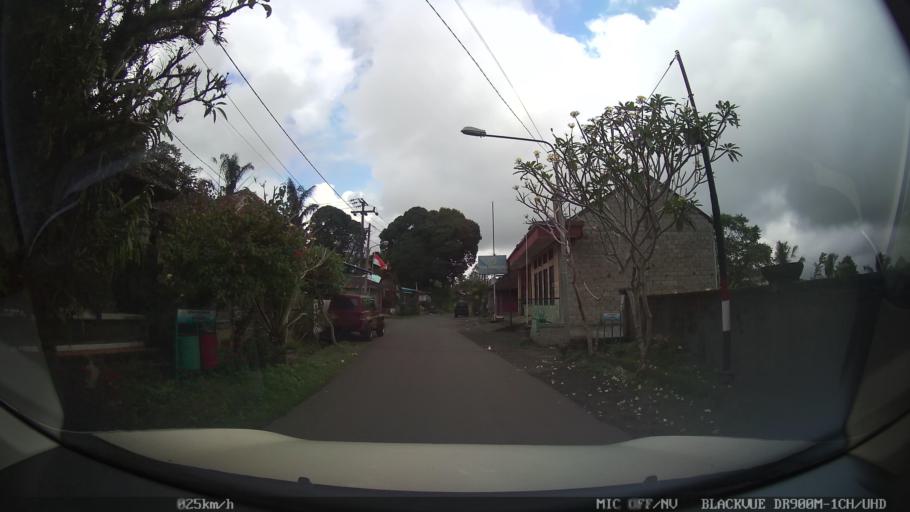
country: ID
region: Bali
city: Peneng
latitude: -8.3513
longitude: 115.2059
